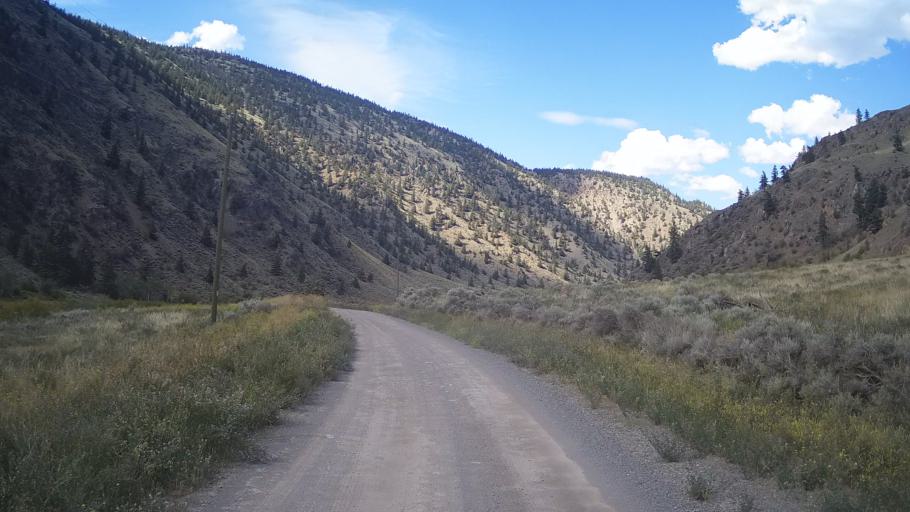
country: CA
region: British Columbia
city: Lillooet
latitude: 51.2089
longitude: -122.0969
